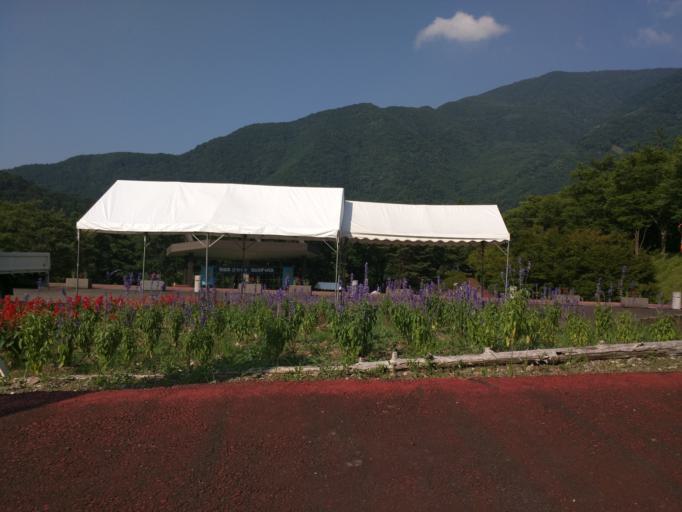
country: JP
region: Fukushima
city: Inawashiro
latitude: 37.3459
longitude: 139.9125
